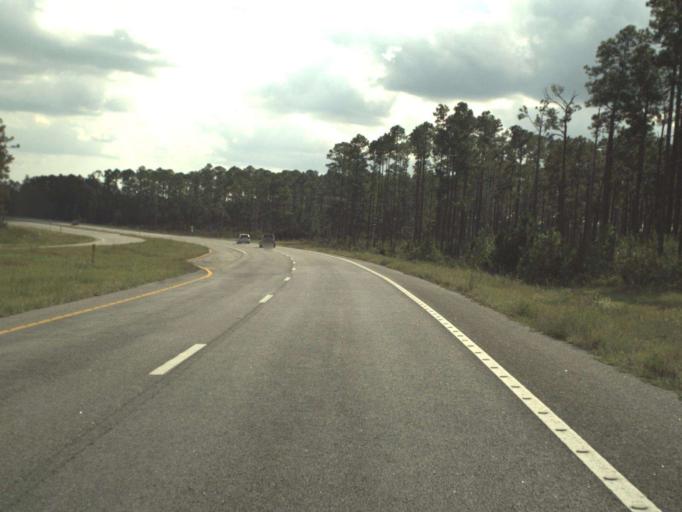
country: US
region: Florida
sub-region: Bay County
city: Laguna Beach
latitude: 30.4252
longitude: -85.8754
